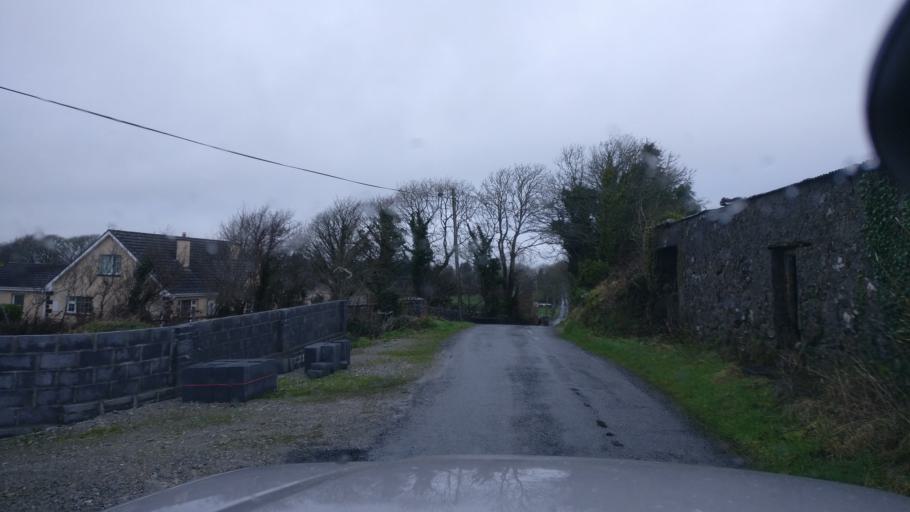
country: IE
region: Connaught
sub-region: County Galway
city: Loughrea
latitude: 53.1642
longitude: -8.6106
